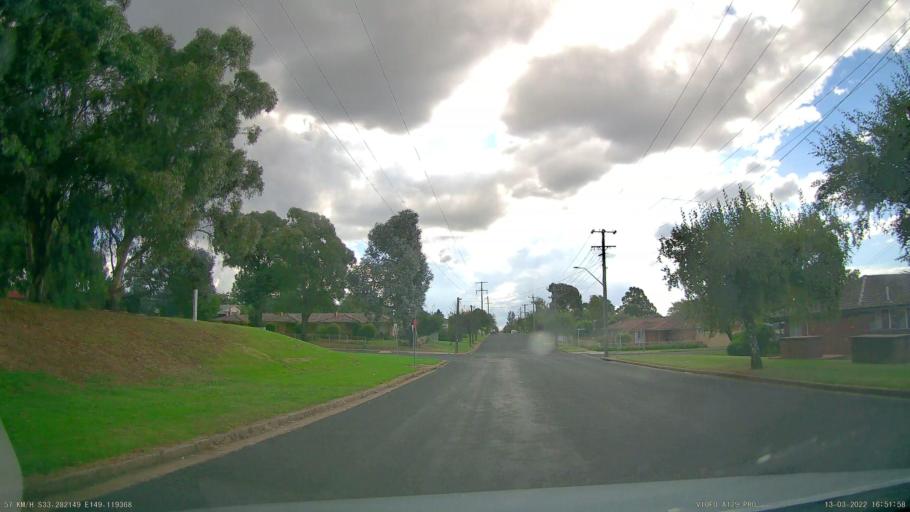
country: AU
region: New South Wales
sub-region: Orange Municipality
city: Orange
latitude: -33.2822
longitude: 149.1190
